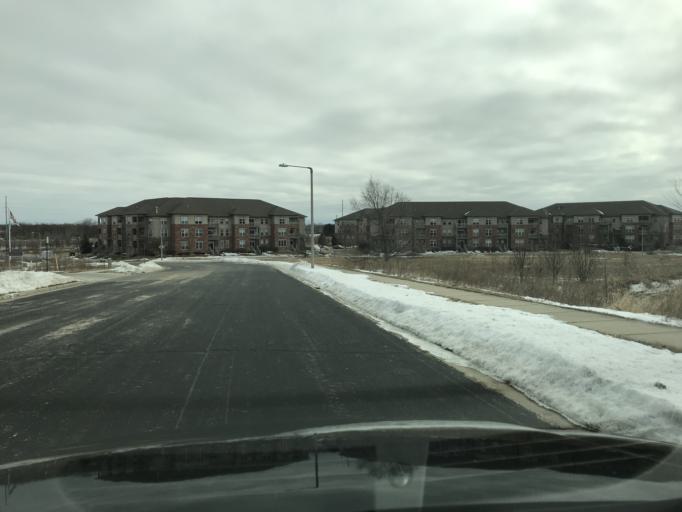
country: US
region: Wisconsin
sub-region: Dane County
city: Monona
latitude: 43.1016
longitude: -89.2709
